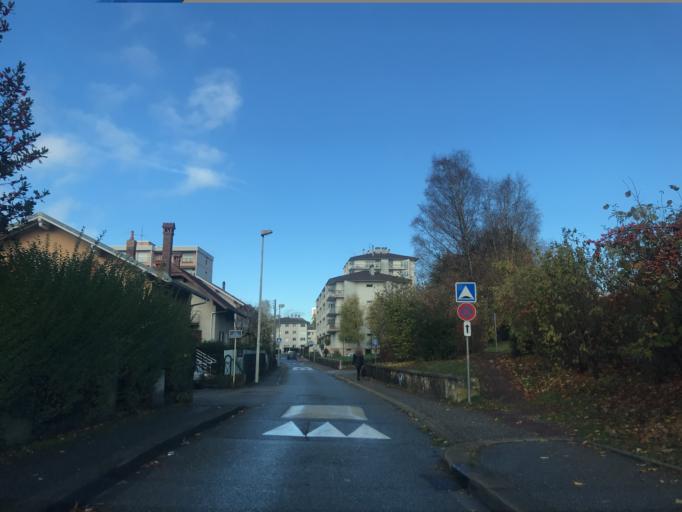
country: FR
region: Rhone-Alpes
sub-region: Departement de la Haute-Savoie
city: Annecy-le-Vieux
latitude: 45.9194
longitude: 6.1351
